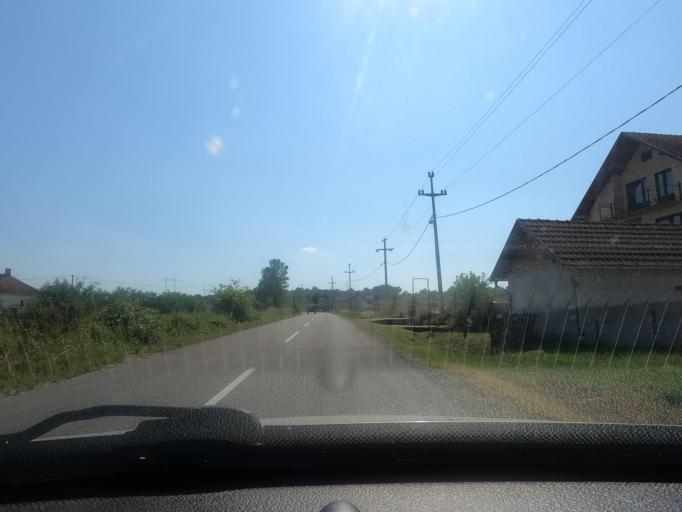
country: RS
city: Kozjak
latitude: 44.5466
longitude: 19.3071
